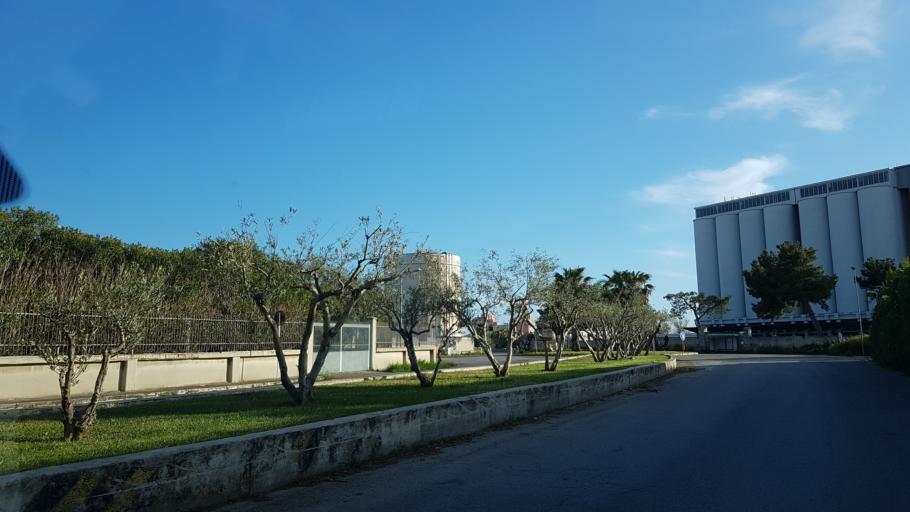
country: IT
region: Apulia
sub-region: Provincia di Brindisi
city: Materdomini
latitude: 40.6396
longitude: 17.9554
